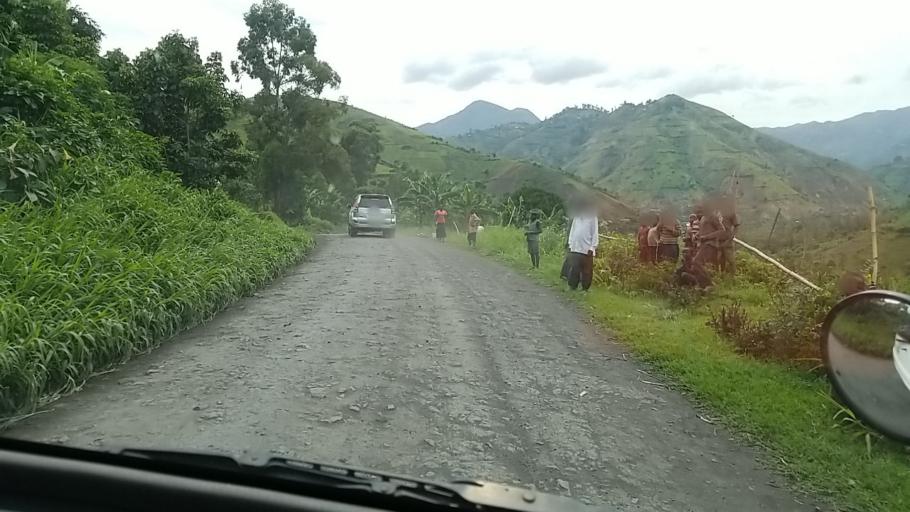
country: CD
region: Nord Kivu
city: Sake
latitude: -1.7405
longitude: 28.9979
